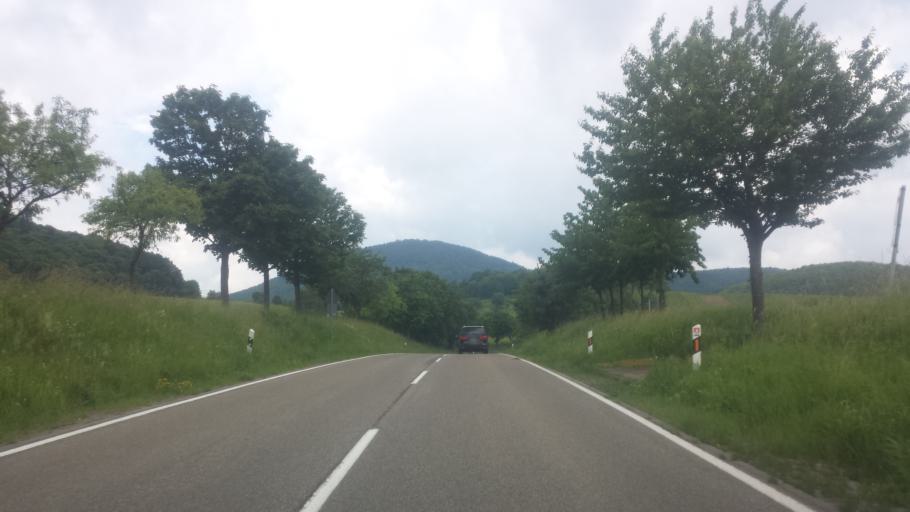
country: DE
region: Rheinland-Pfalz
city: Ranschbach
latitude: 49.1892
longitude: 8.0276
